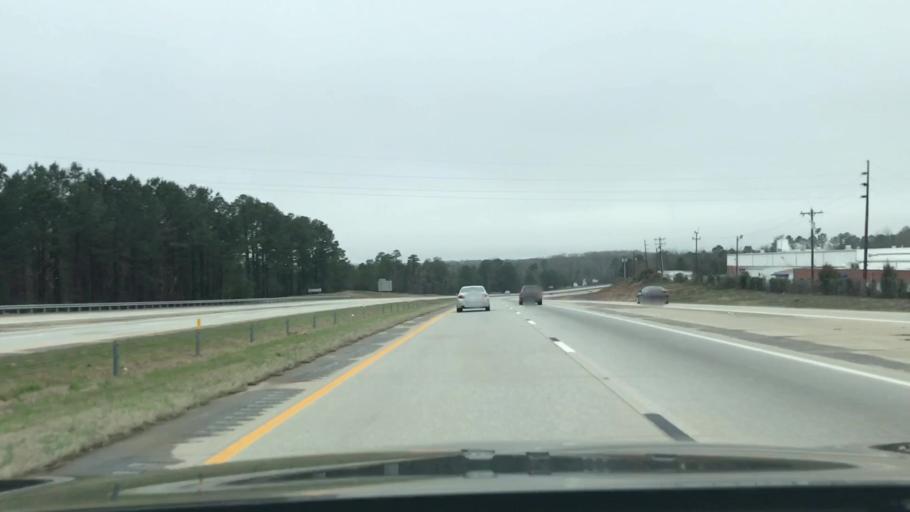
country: US
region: South Carolina
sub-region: Laurens County
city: Watts Mills
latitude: 34.5537
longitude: -82.0087
